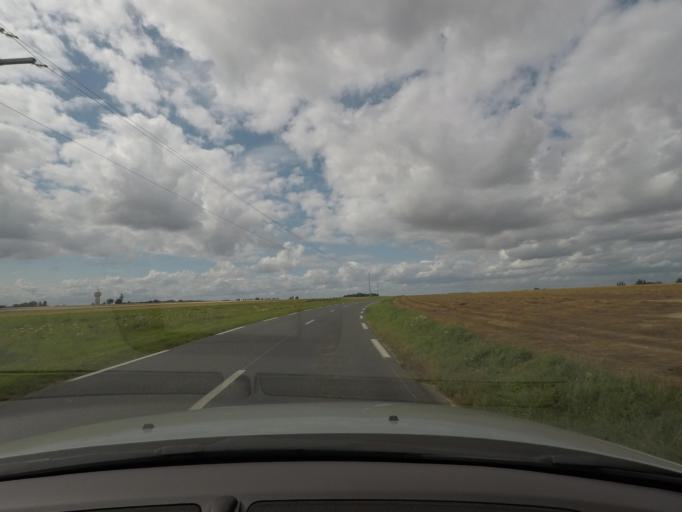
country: FR
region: Haute-Normandie
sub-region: Departement de l'Eure
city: Les Andelys
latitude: 49.2275
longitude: 1.4375
